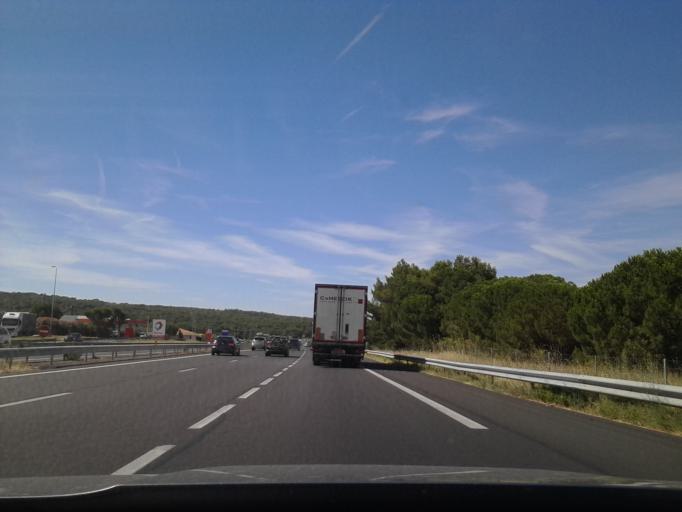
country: FR
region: Languedoc-Roussillon
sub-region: Departement de l'Aude
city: Vinassan
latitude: 43.2183
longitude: 3.0926
